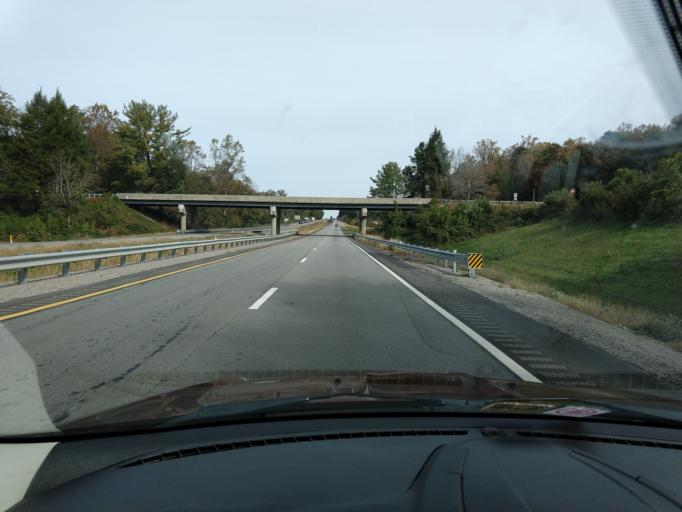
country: US
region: Virginia
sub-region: Pittsylvania County
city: Chatham
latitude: 36.8261
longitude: -79.3809
